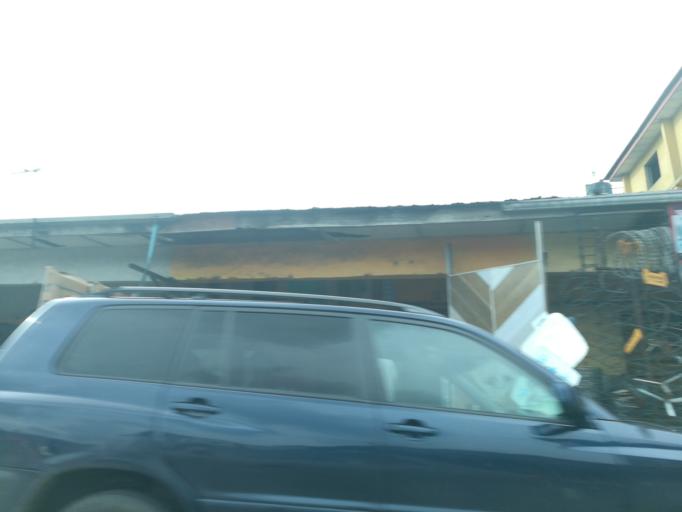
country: NG
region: Rivers
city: Port Harcourt
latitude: 4.8062
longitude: 6.9897
